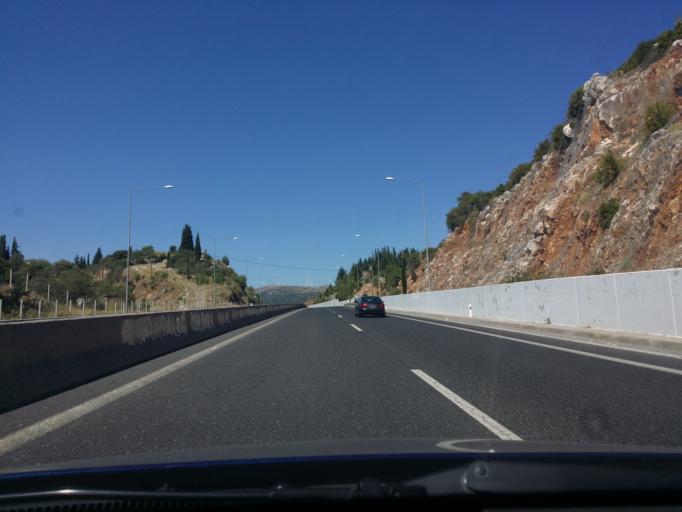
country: GR
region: Peloponnese
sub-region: Nomos Arkadias
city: Tripoli
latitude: 37.4868
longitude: 22.3595
